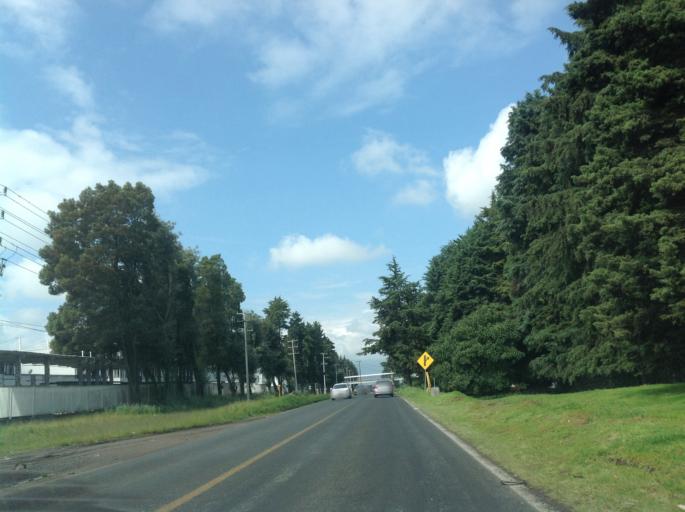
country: MX
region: Mexico
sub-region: Tianguistenco
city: San Jose Mezapa Seccion I
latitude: 19.1686
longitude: -99.4556
